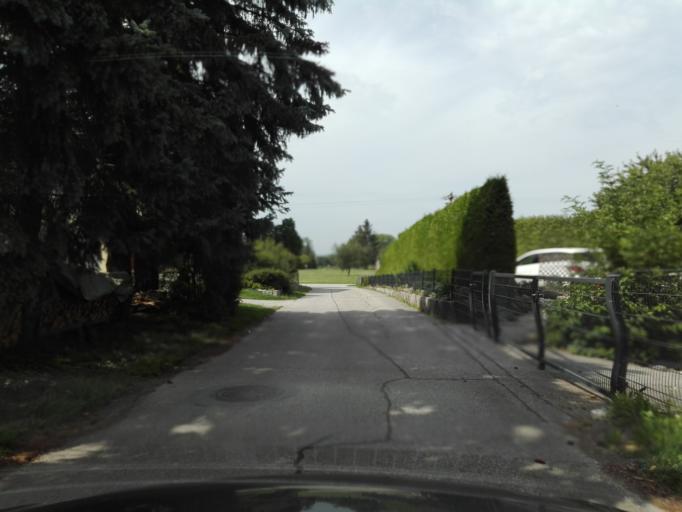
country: AT
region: Lower Austria
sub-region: Politischer Bezirk Amstetten
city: Strengberg
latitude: 48.1796
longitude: 14.6813
